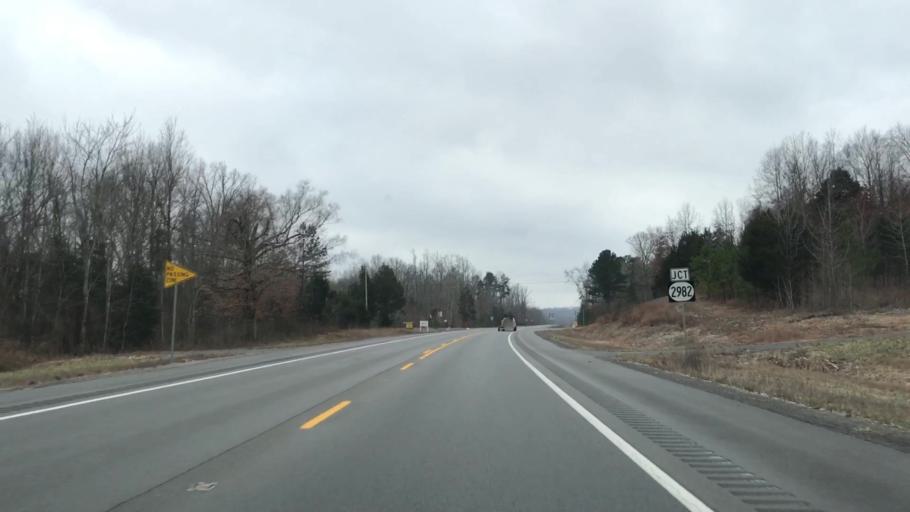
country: US
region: Kentucky
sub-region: Adair County
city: Columbia
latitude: 37.0503
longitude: -85.3627
